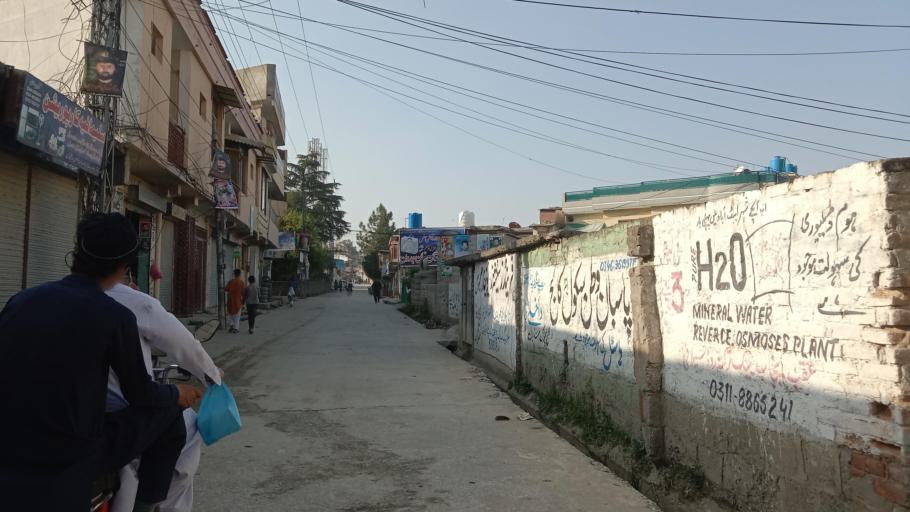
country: PK
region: Khyber Pakhtunkhwa
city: Abbottabad
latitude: 34.1988
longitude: 73.2283
